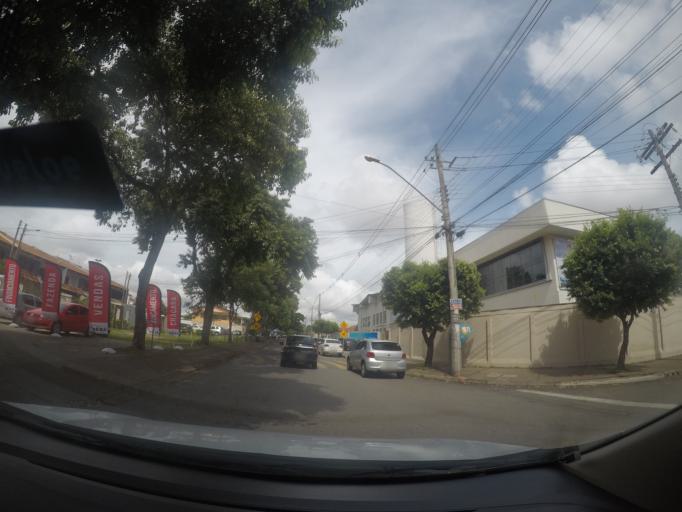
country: BR
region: Goias
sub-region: Goiania
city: Goiania
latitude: -16.7143
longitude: -49.3025
